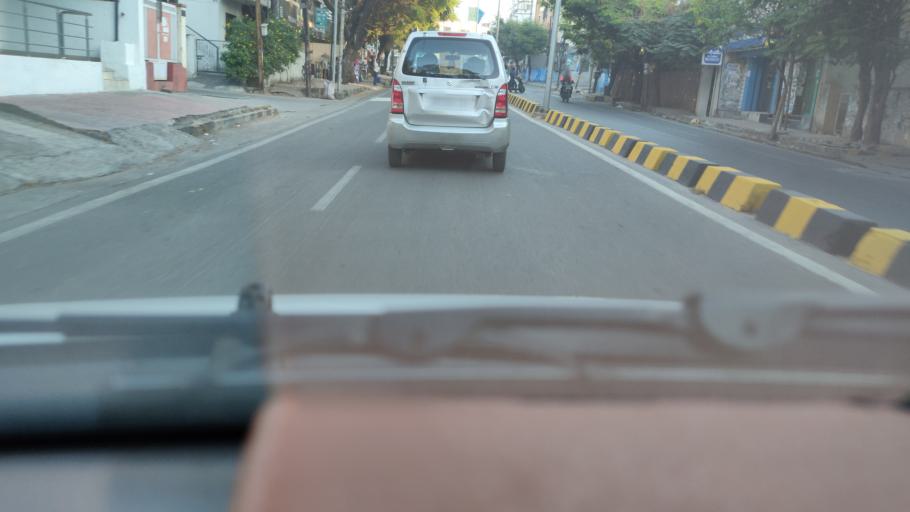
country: IN
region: Telangana
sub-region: Rangareddi
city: Gaddi Annaram
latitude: 17.4038
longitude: 78.5148
